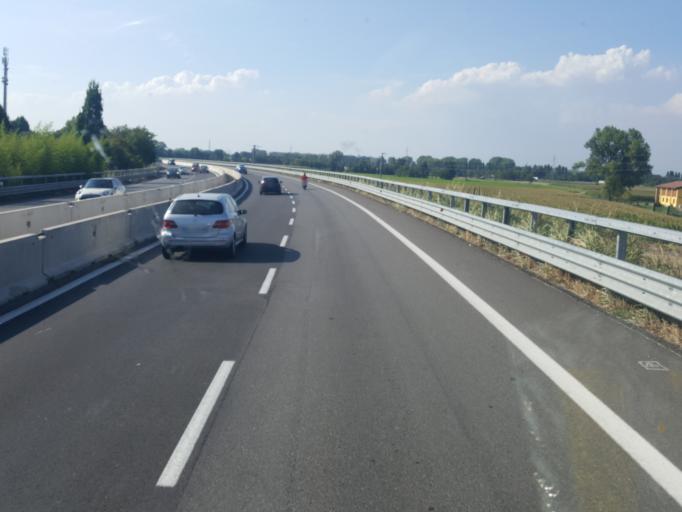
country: IT
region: Lombardy
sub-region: Citta metropolitana di Milano
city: Opera
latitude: 45.3780
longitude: 9.2269
